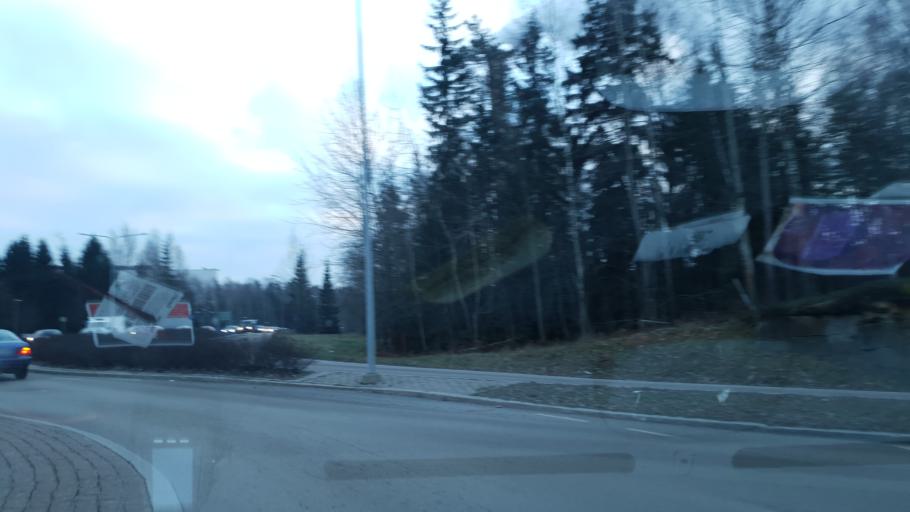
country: FI
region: Uusimaa
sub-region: Helsinki
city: Teekkarikylae
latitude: 60.2361
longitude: 24.8887
